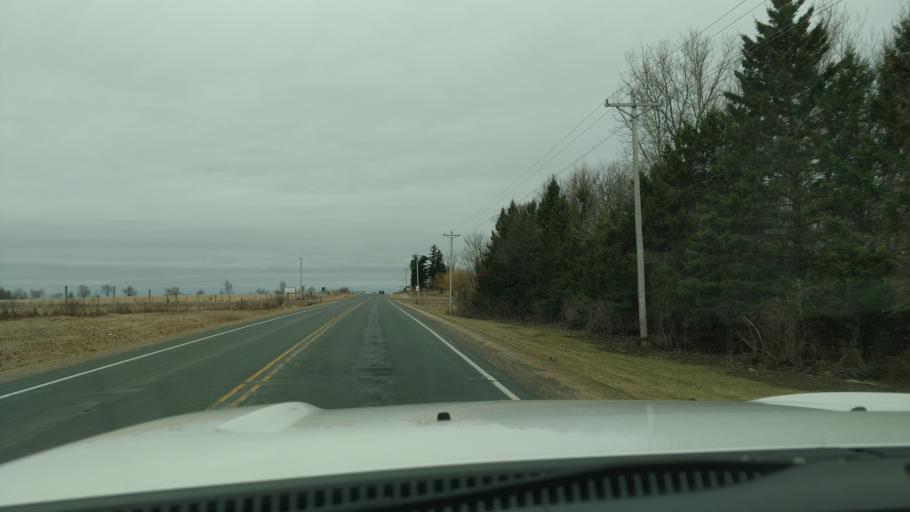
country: US
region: Wisconsin
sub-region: Saint Croix County
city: Hammond
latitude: 44.9359
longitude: -92.4356
